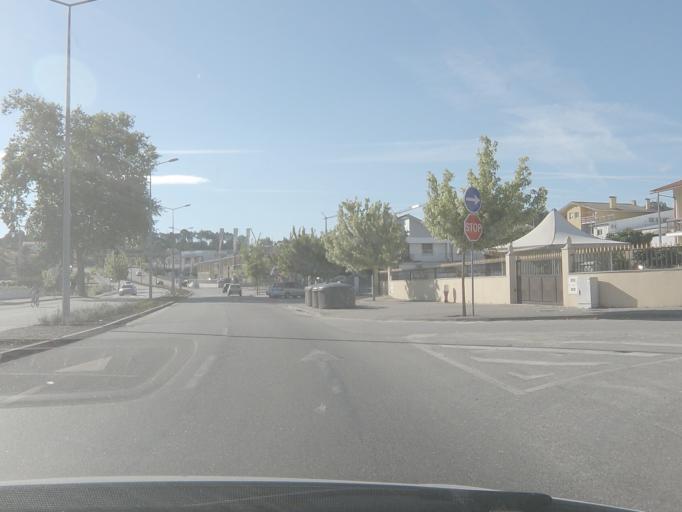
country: PT
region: Viseu
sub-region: Viseu
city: Abraveses
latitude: 40.6914
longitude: -7.9272
